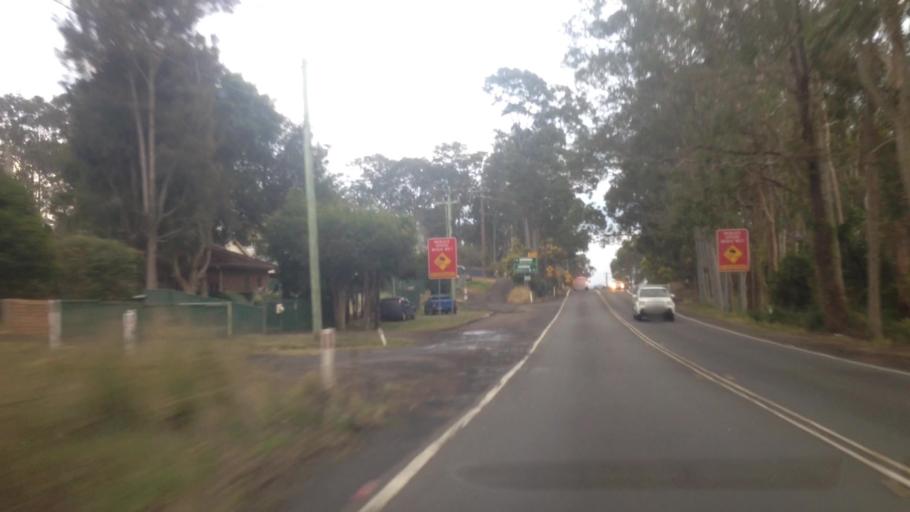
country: AU
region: New South Wales
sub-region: Wyong Shire
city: Jilliby
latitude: -33.2700
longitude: 151.4314
